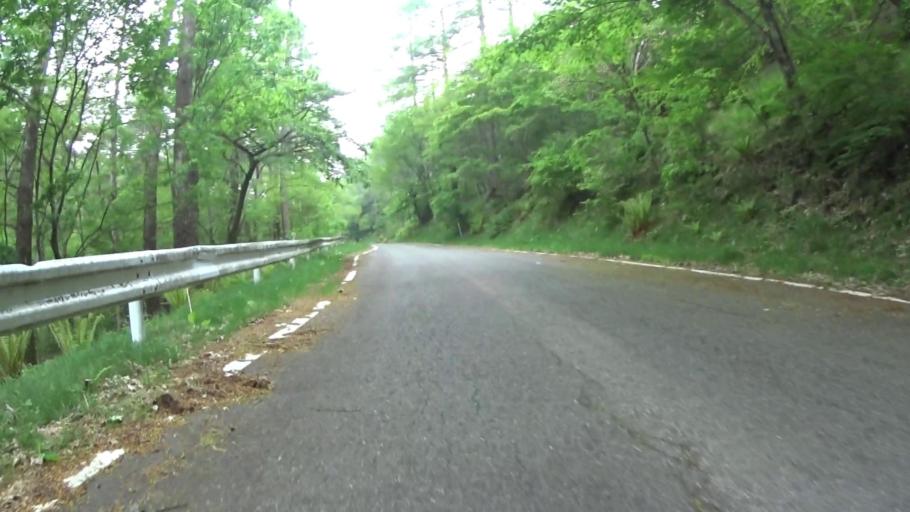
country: JP
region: Yamanashi
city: Kofu-shi
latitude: 35.8326
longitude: 138.5678
